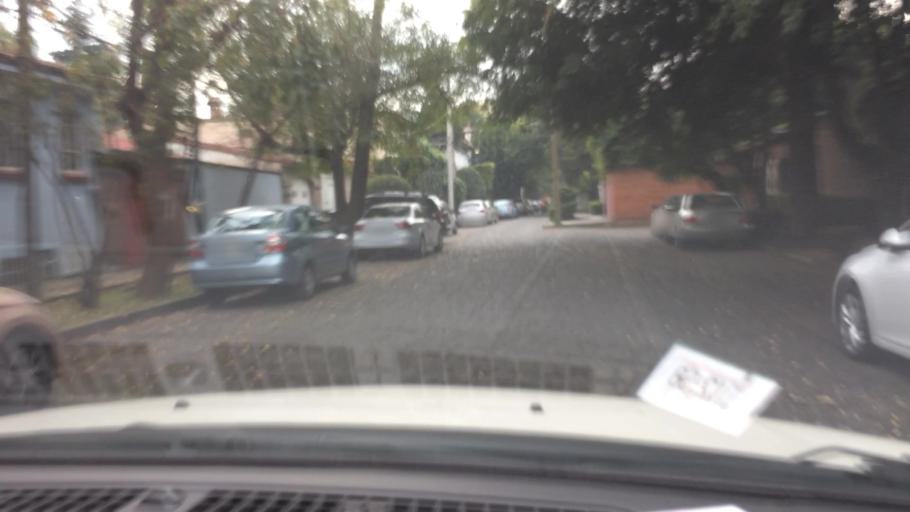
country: MX
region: Mexico City
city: Alvaro Obregon
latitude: 19.3523
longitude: -99.1916
